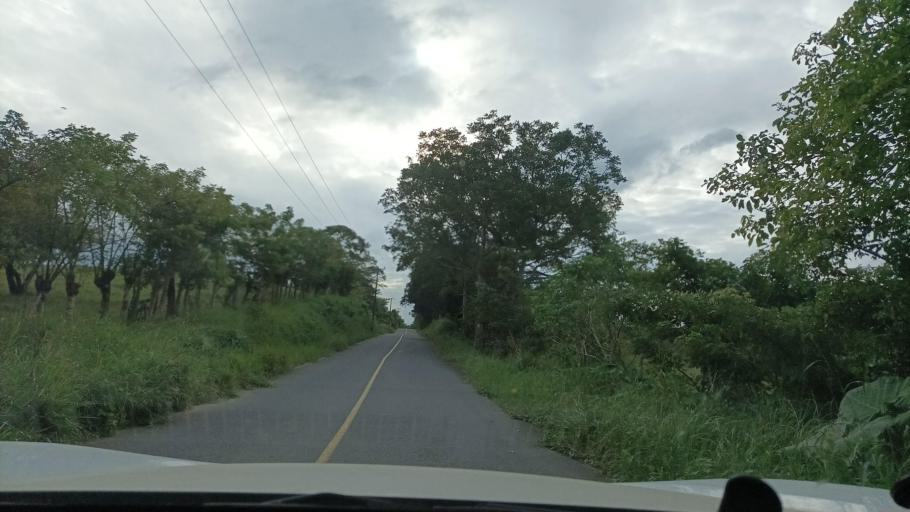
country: MX
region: Veracruz
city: Hidalgotitlan
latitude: 17.7176
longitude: -94.4771
